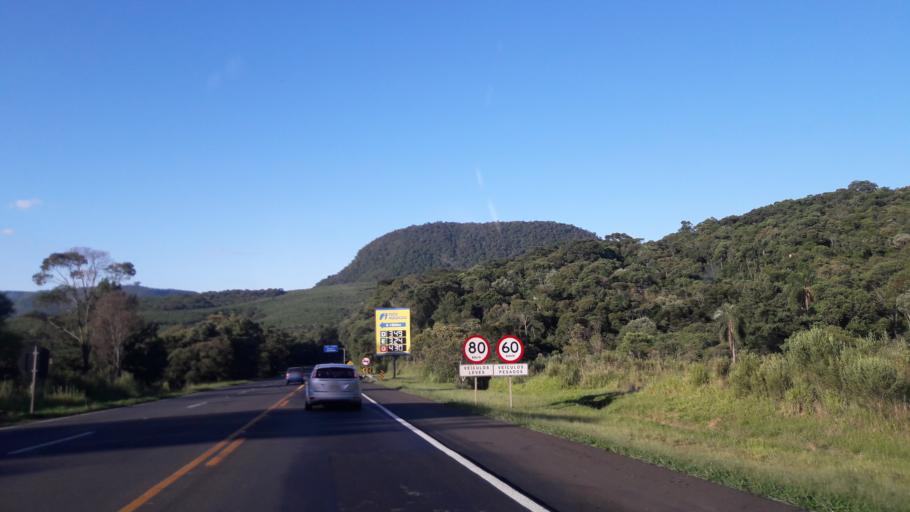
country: BR
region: Parana
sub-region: Prudentopolis
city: Prudentopolis
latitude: -25.3172
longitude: -51.1889
